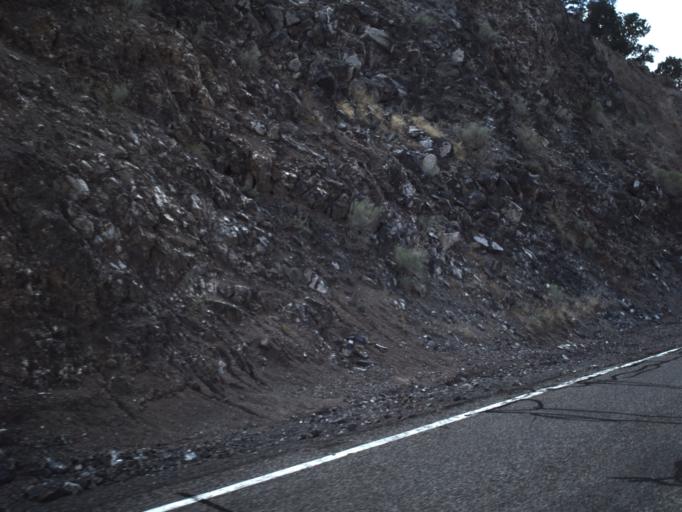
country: US
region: Utah
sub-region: Sevier County
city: Richfield
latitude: 38.7780
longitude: -111.9417
